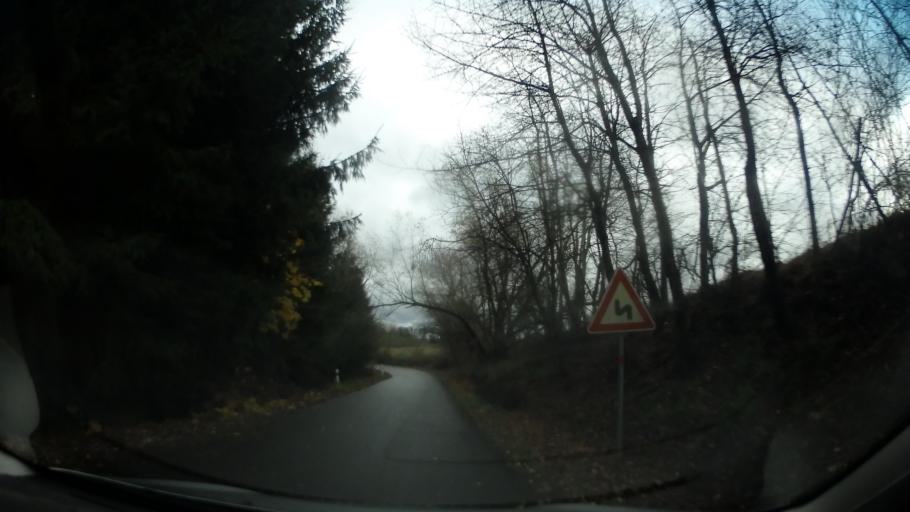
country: CZ
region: Vysocina
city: Namest' nad Oslavou
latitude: 49.2875
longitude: 16.1162
